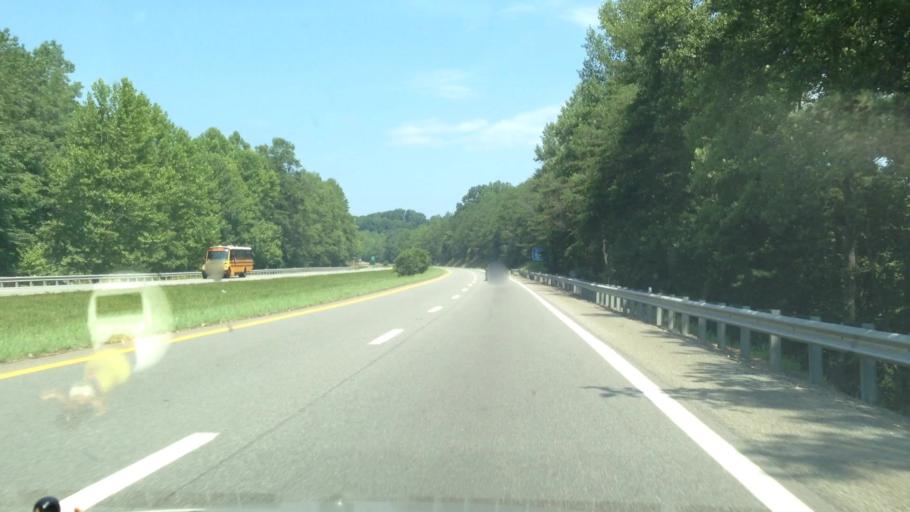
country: US
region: Virginia
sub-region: Henry County
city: Collinsville
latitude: 36.6867
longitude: -79.9411
